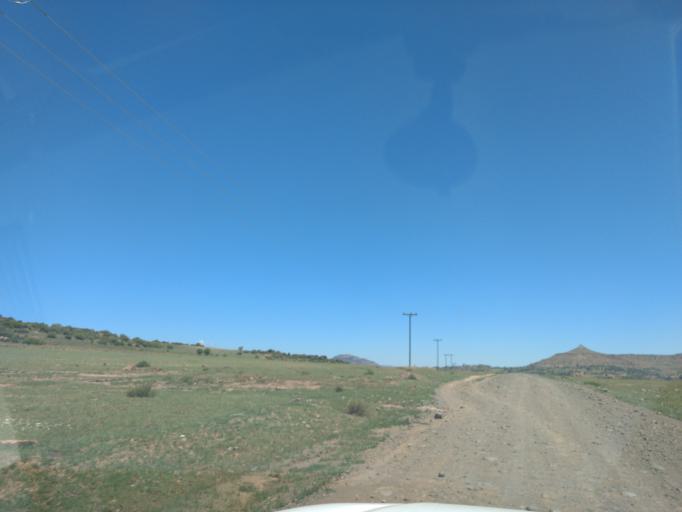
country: LS
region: Maseru
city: Maseru
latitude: -29.4673
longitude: 27.3759
